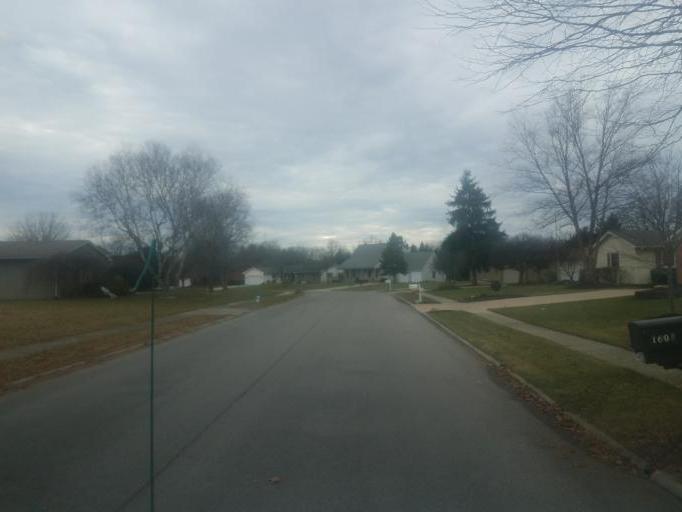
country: US
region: Ohio
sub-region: Marion County
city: Marion
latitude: 40.5728
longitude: -83.0827
